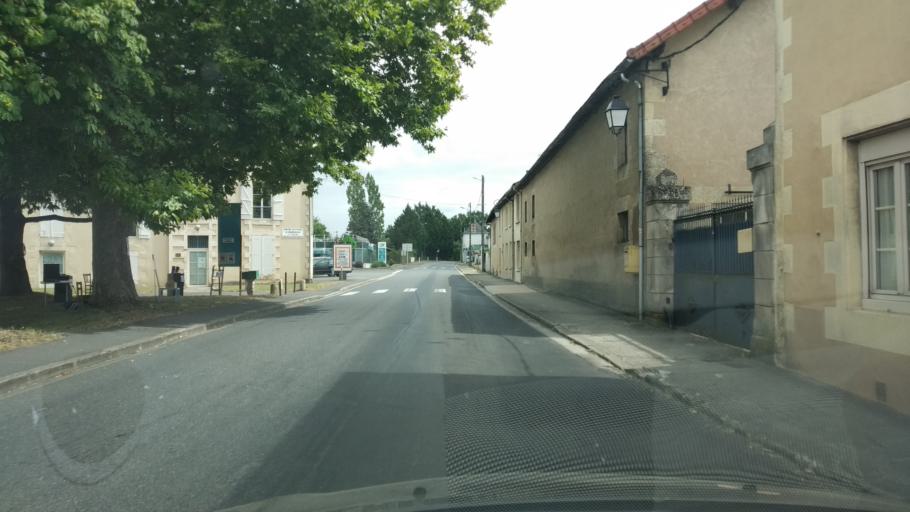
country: FR
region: Poitou-Charentes
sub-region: Departement de la Vienne
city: Saint-Maurice-la-Clouere
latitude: 46.3719
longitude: 0.4058
